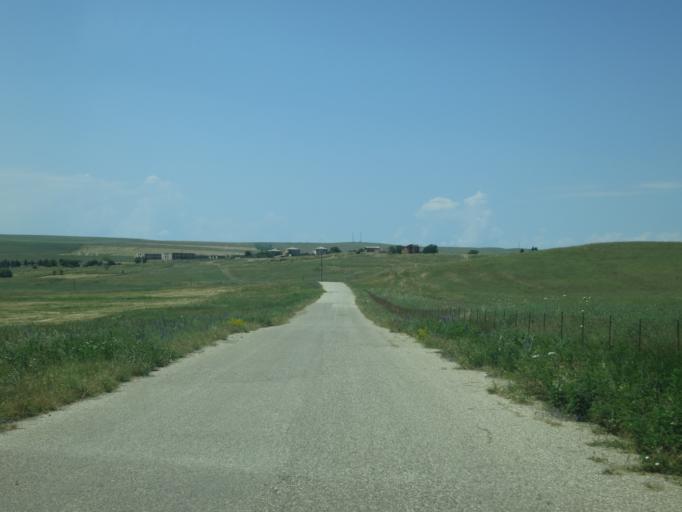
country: GE
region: Kakheti
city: Sagarejo
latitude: 41.5096
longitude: 45.3896
